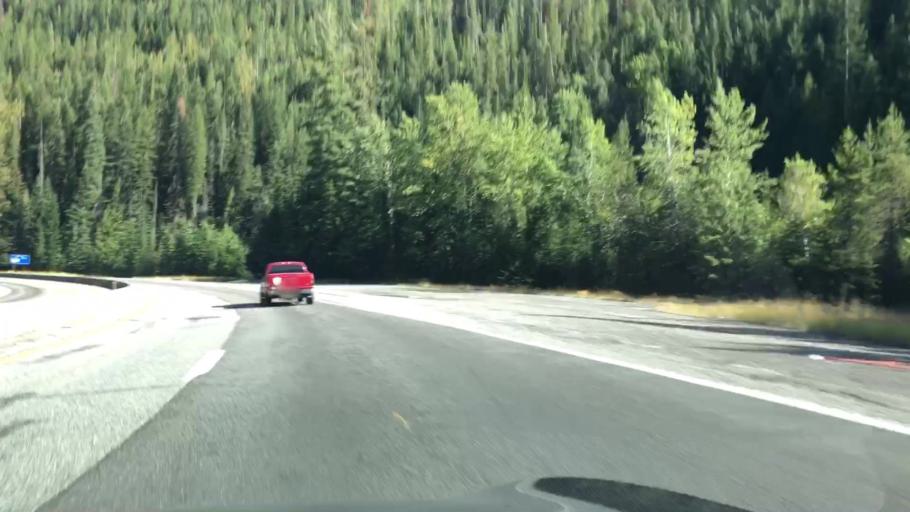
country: US
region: Idaho
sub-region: Shoshone County
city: Wallace
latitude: 47.4634
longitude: -115.8088
